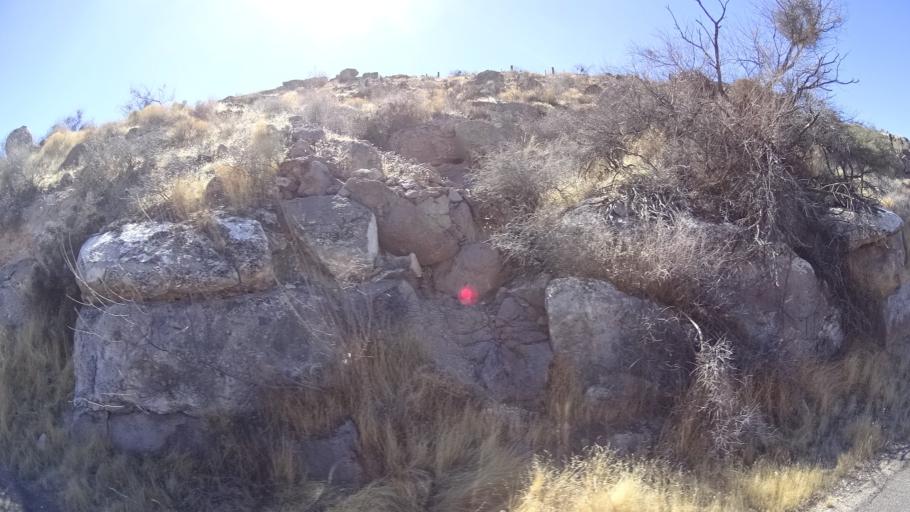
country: US
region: Arizona
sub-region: Mohave County
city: Kingman
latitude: 35.1819
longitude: -114.0606
